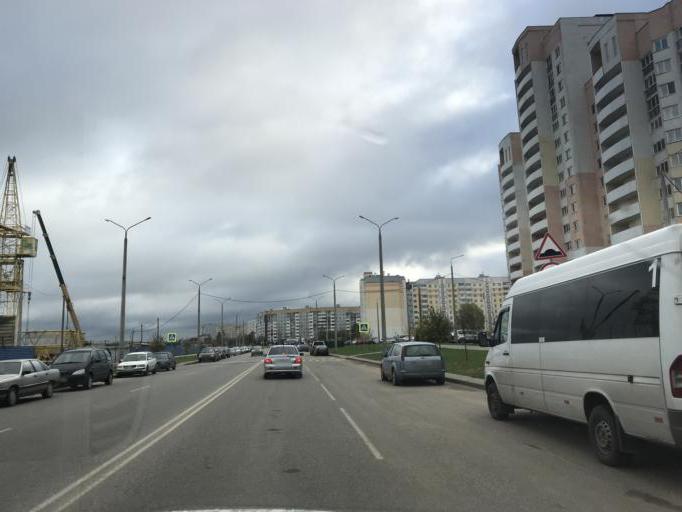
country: BY
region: Mogilev
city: Mahilyow
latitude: 53.8826
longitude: 30.3617
